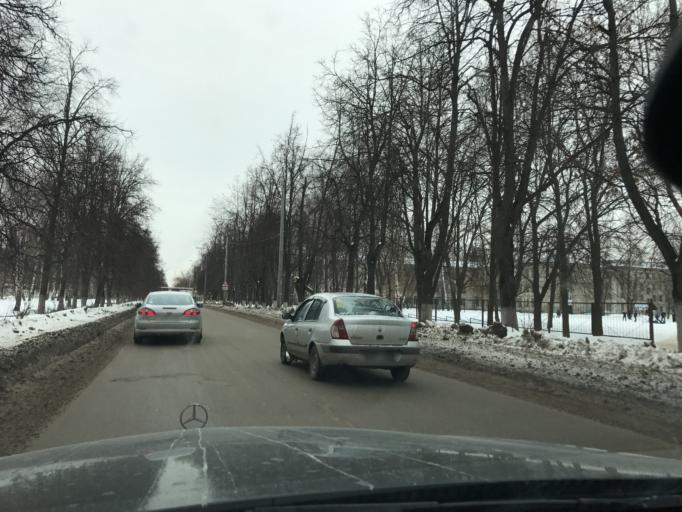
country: RU
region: Nizjnij Novgorod
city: Gorbatovka
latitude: 56.2475
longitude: 43.8356
